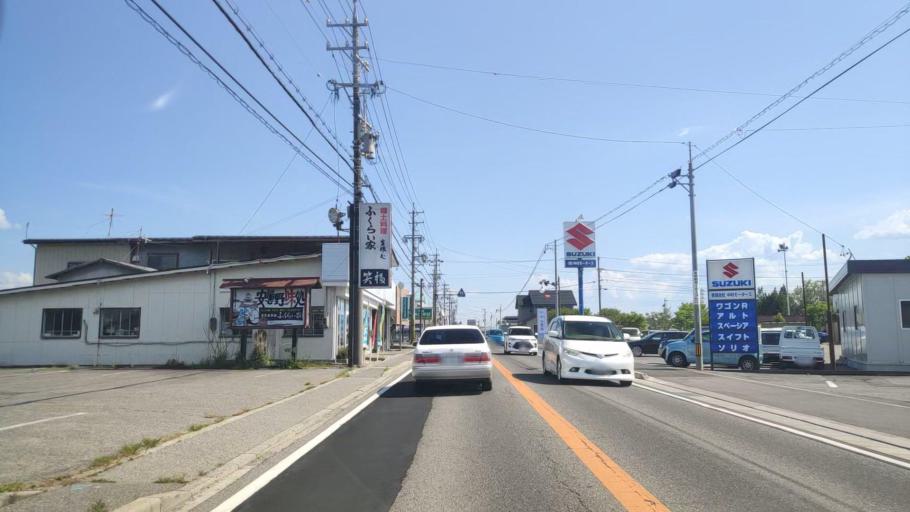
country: JP
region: Nagano
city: Hotaka
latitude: 36.3436
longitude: 137.8867
